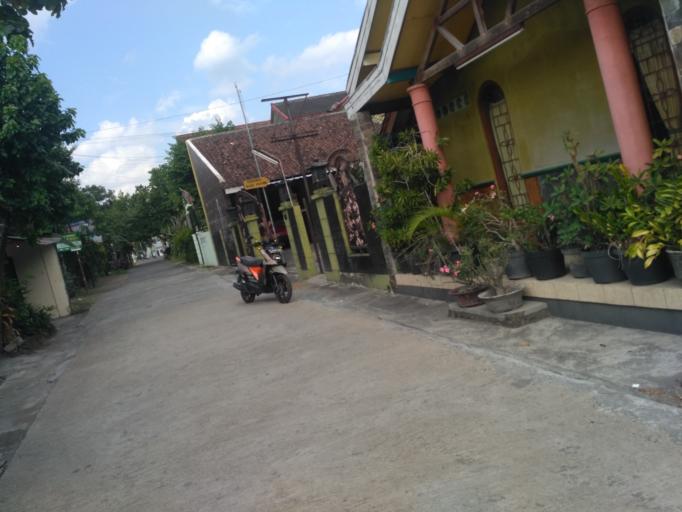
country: ID
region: Daerah Istimewa Yogyakarta
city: Depok
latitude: -7.7748
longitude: 110.4049
